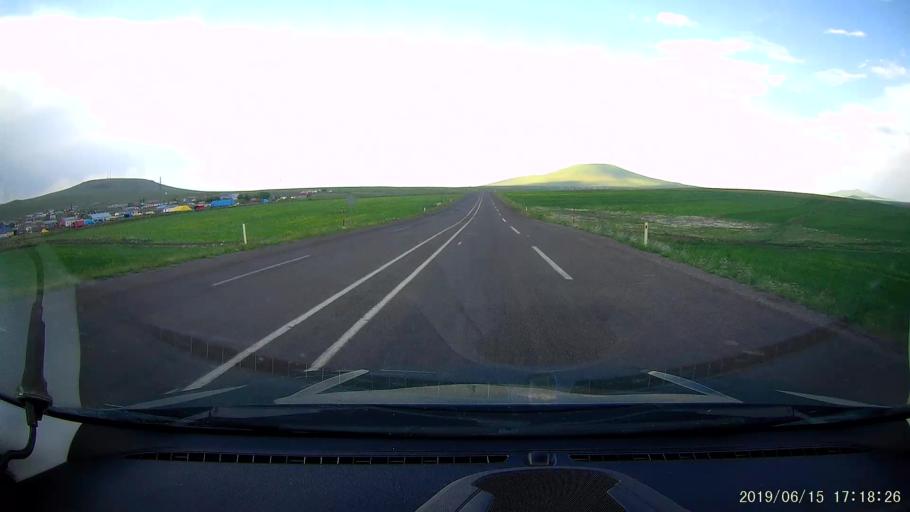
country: TR
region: Kars
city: Kars
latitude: 40.6128
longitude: 43.2581
